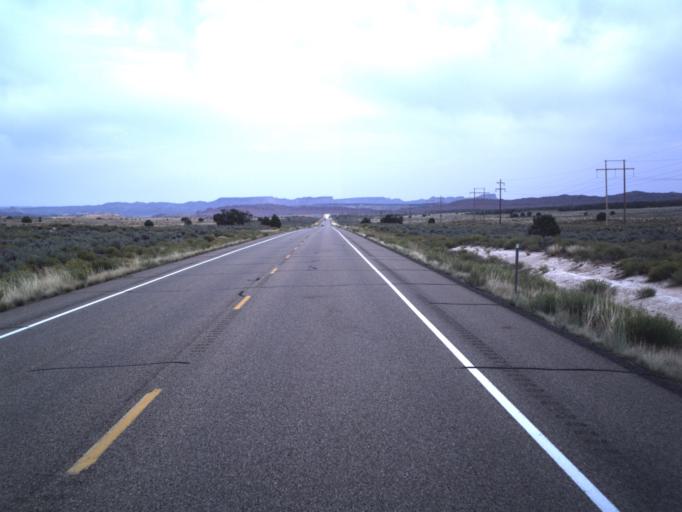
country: US
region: Utah
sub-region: Kane County
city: Kanab
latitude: 37.1628
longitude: -112.0405
